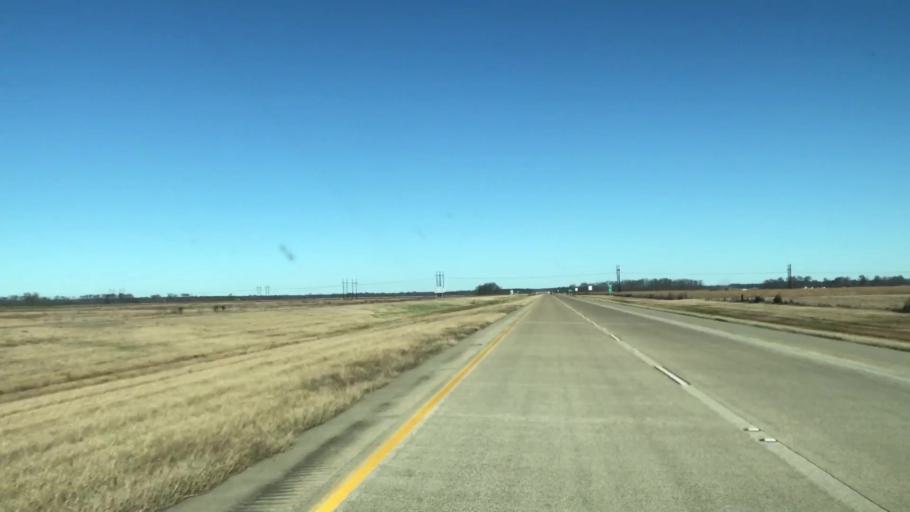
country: US
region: Louisiana
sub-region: Caddo Parish
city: Oil City
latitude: 32.7107
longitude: -93.8648
